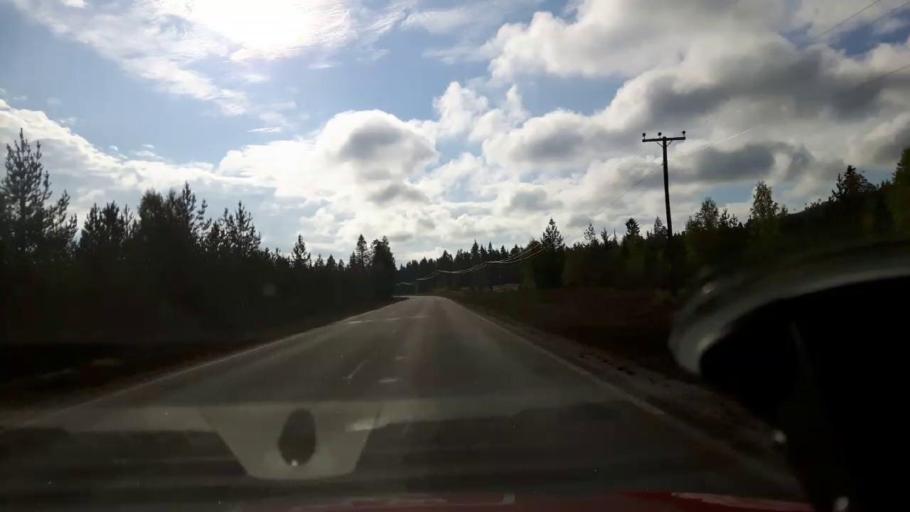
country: SE
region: Jaemtland
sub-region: Harjedalens Kommun
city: Sveg
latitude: 62.1054
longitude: 15.0665
